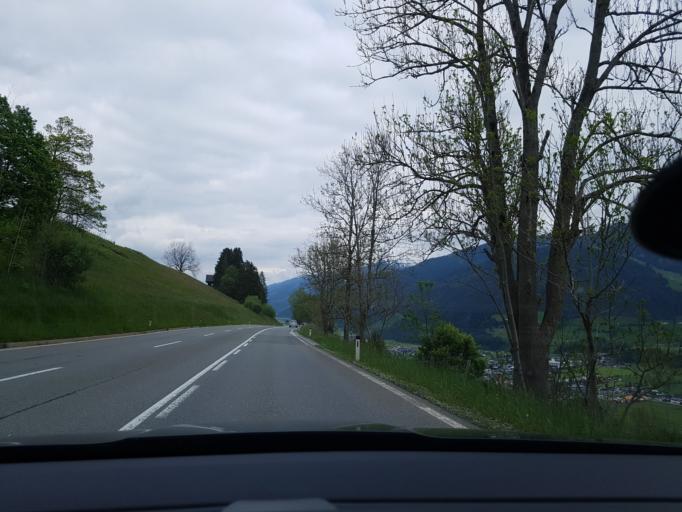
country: AT
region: Salzburg
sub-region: Politischer Bezirk Zell am See
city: Mittersill
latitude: 47.2884
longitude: 12.4627
